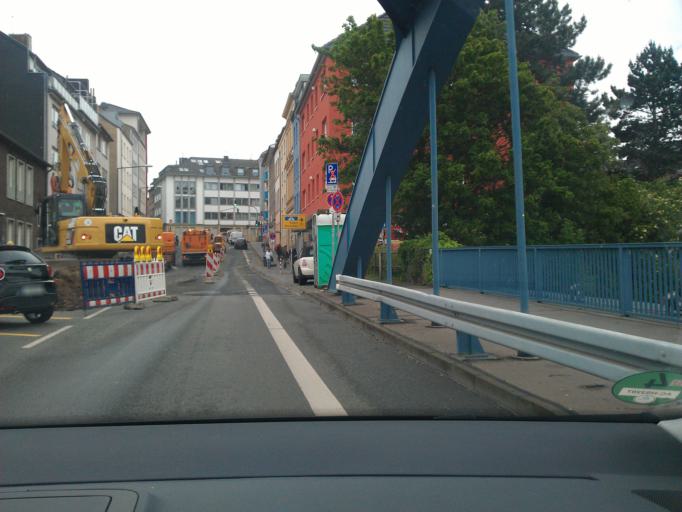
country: DE
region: North Rhine-Westphalia
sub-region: Regierungsbezirk Koln
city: Aachen
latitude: 50.7663
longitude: 6.0880
